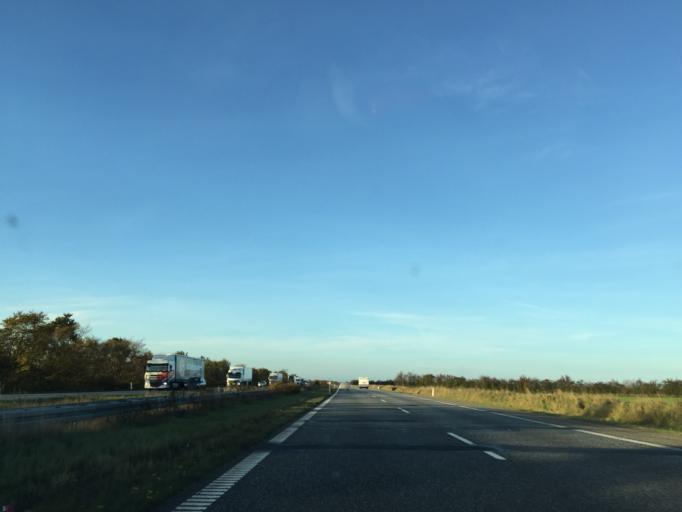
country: DK
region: South Denmark
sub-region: Aabenraa Kommune
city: Krusa
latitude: 54.8845
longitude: 9.3787
